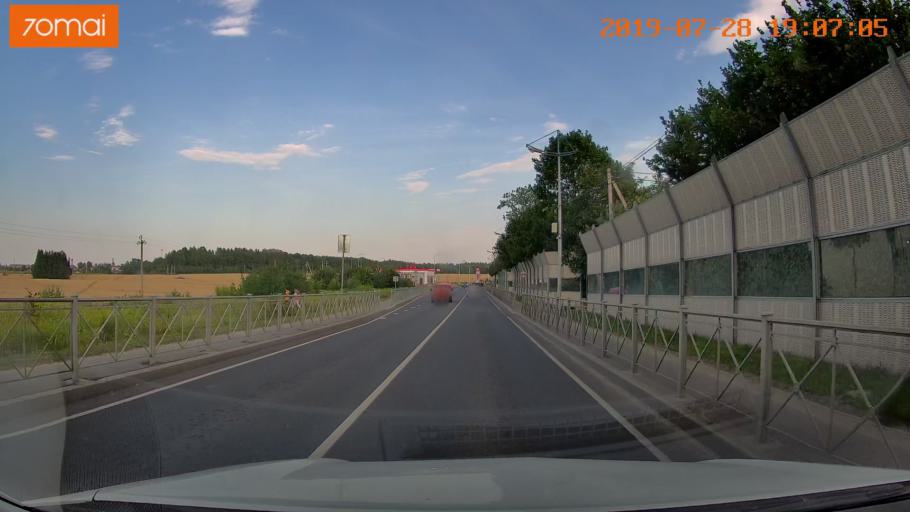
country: RU
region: Kaliningrad
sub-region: Gorod Svetlogorsk
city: Svetlogorsk
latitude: 54.9289
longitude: 20.1691
